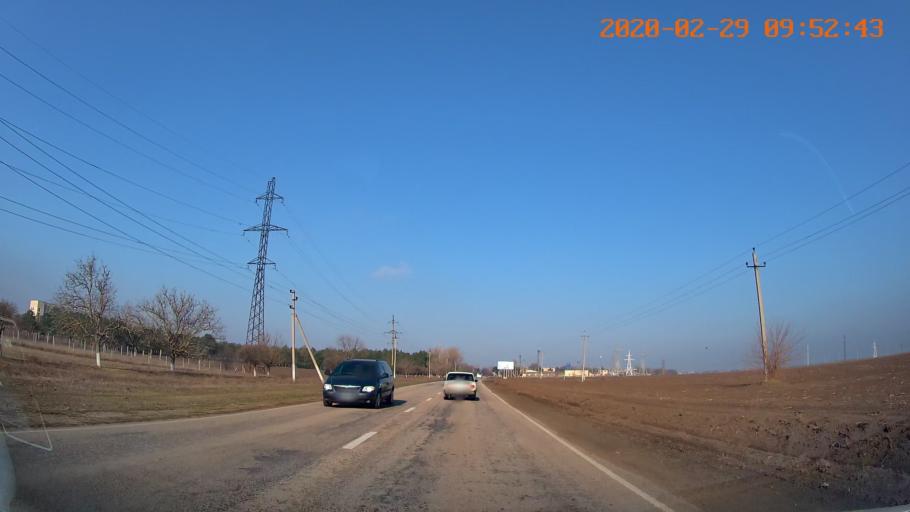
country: MD
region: Telenesti
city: Slobozia
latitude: 46.7176
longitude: 29.7279
